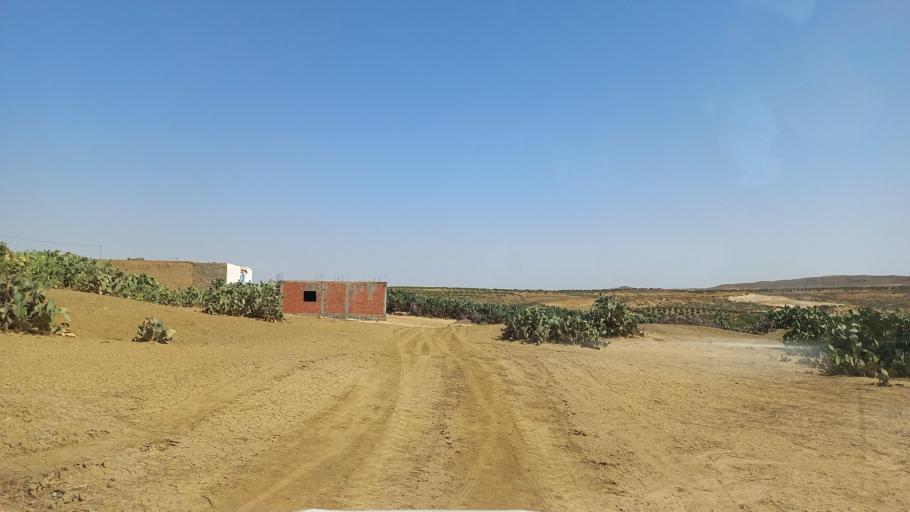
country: TN
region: Al Qasrayn
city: Kasserine
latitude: 35.1999
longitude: 9.0351
